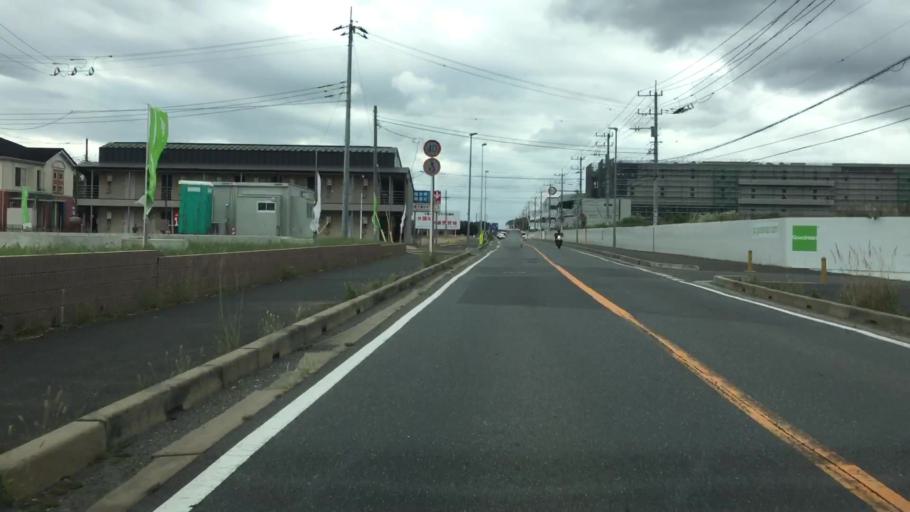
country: JP
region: Chiba
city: Shiroi
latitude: 35.8190
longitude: 140.1361
